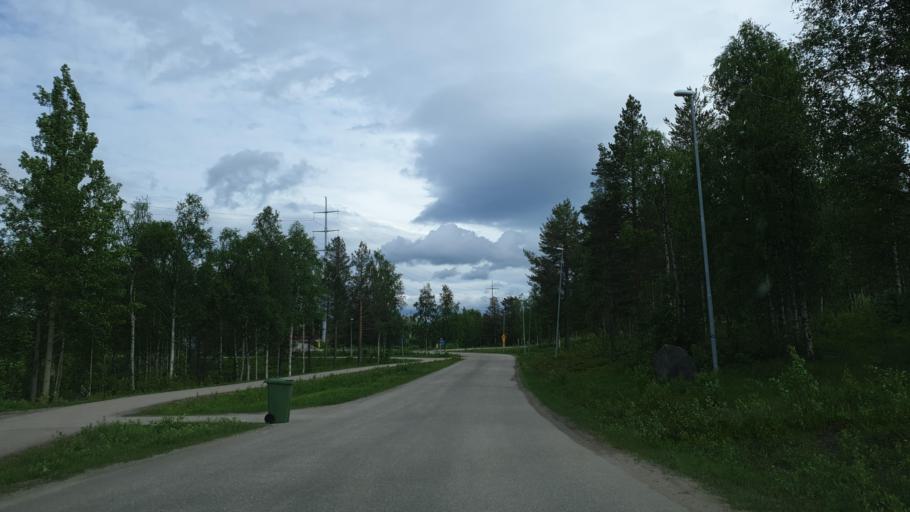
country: SE
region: Norrbotten
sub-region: Gallivare Kommun
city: Gaellivare
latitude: 67.1274
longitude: 20.6546
